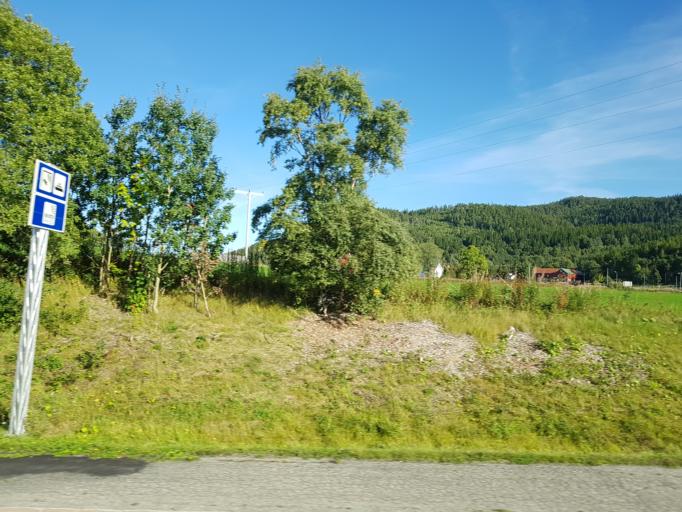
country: NO
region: Sor-Trondelag
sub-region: Skaun
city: Borsa
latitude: 63.4468
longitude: 10.1921
